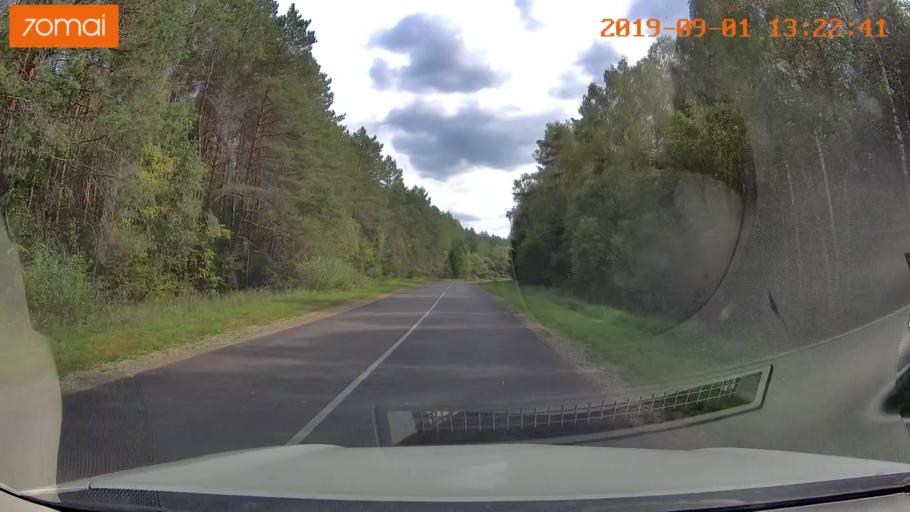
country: RU
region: Kaluga
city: Maloyaroslavets
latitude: 54.8875
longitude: 36.5260
